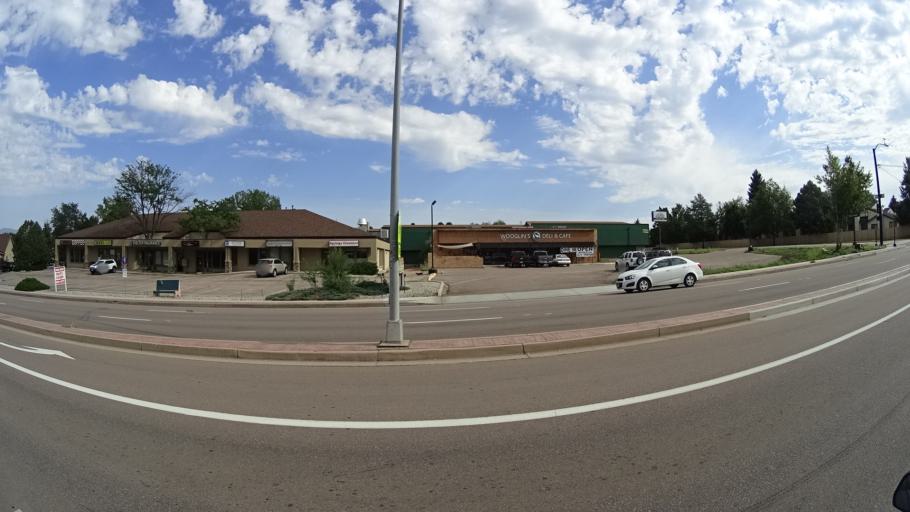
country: US
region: Colorado
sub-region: El Paso County
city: Cimarron Hills
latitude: 38.8968
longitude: -104.7390
